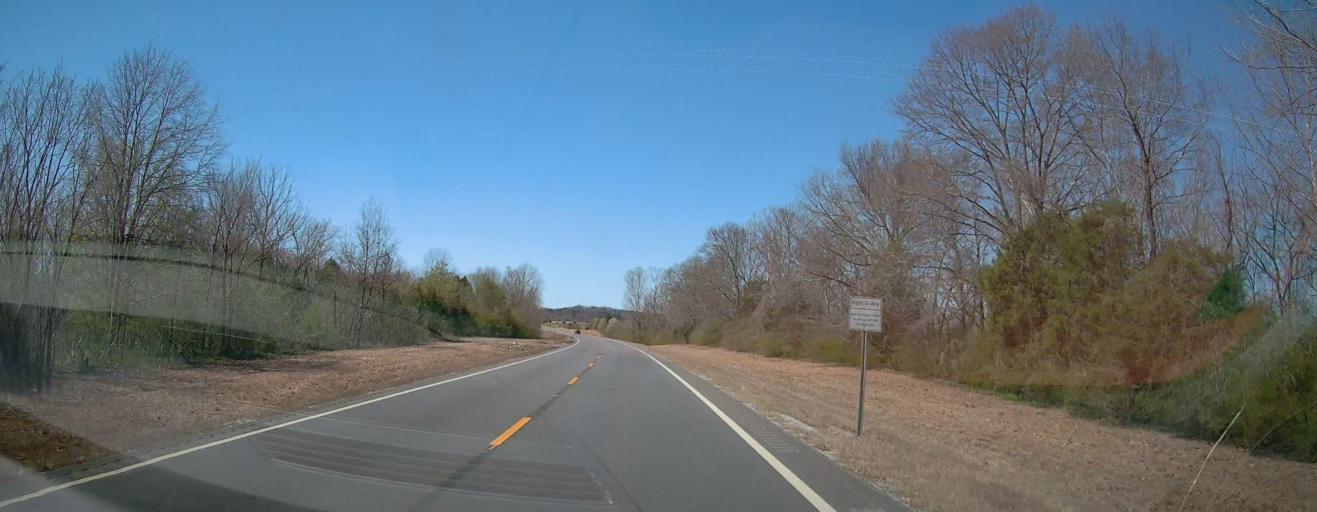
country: US
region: Alabama
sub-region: Calhoun County
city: Alexandria
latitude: 33.7847
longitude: -85.9253
